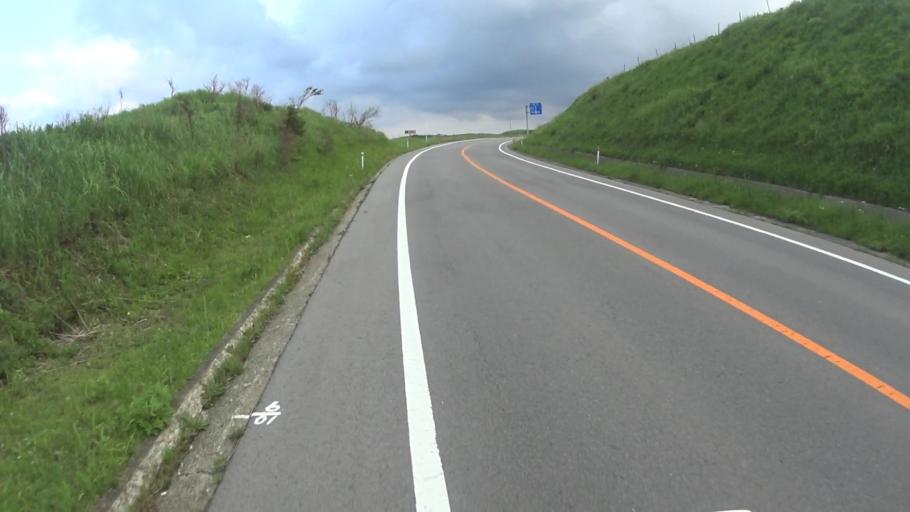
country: JP
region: Kumamoto
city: Aso
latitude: 32.9986
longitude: 131.0166
